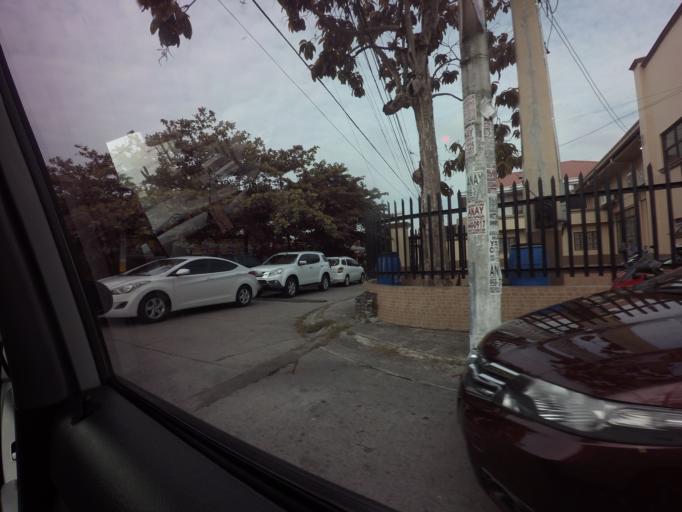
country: PH
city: Sambayanihan People's Village
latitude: 14.4444
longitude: 121.0287
